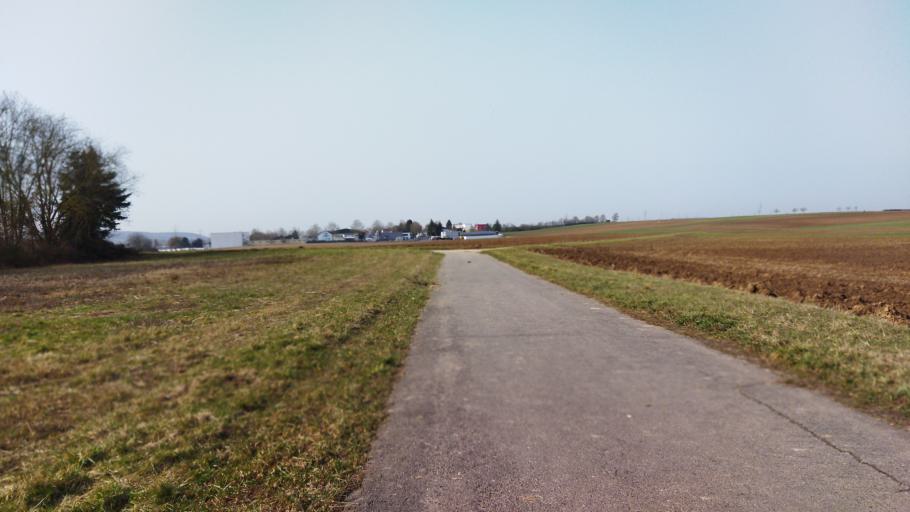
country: DE
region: Baden-Wuerttemberg
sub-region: Regierungsbezirk Stuttgart
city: Heilbronn
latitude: 49.1421
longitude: 9.1754
